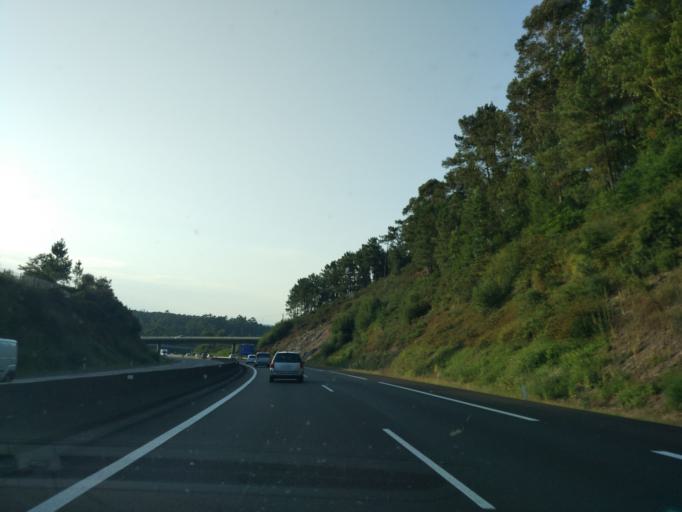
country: ES
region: Galicia
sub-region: Provincia de Pontevedra
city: Portas
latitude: 42.5533
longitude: -8.6684
